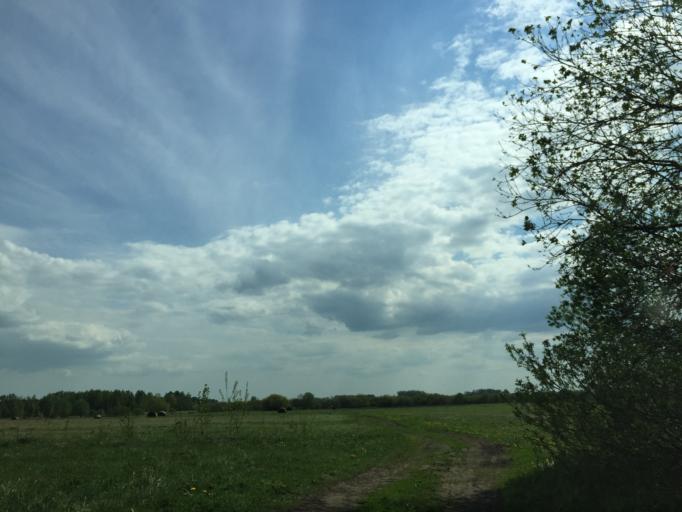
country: LV
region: Jelgava
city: Jelgava
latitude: 56.7289
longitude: 23.6764
